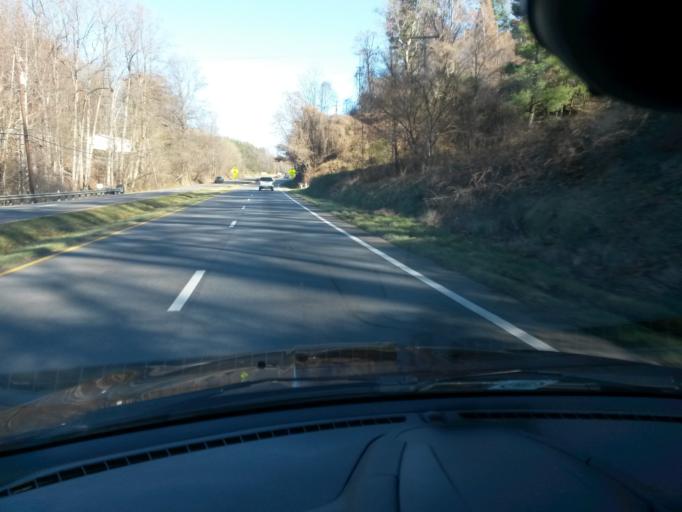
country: US
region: Virginia
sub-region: Roanoke County
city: Narrows
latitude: 37.1490
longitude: -79.9626
